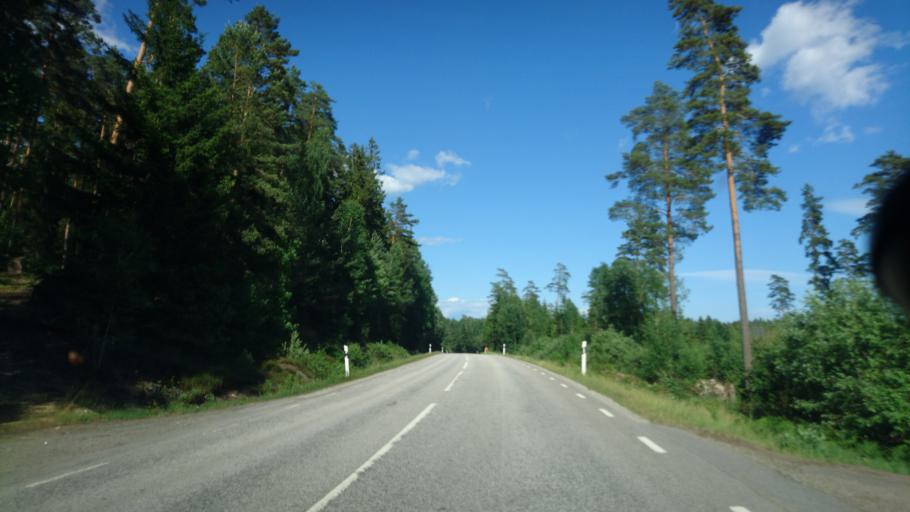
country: SE
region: Skane
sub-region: Osby Kommun
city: Lonsboda
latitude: 56.3910
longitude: 14.4293
